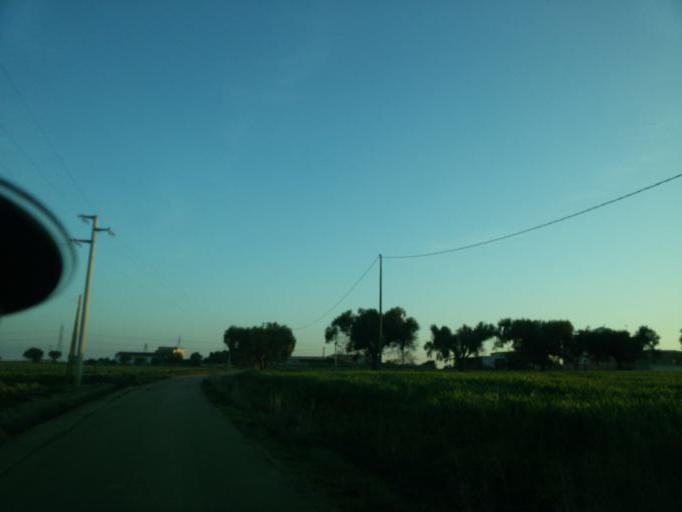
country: IT
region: Apulia
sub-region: Provincia di Brindisi
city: La Rosa
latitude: 40.6051
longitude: 17.9390
